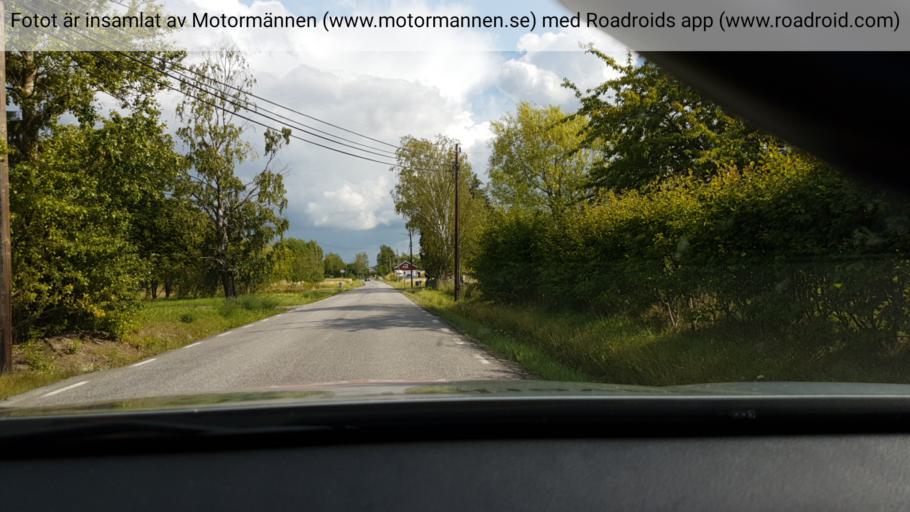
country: SE
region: Stockholm
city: Stenhamra
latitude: 59.4011
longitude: 17.6452
